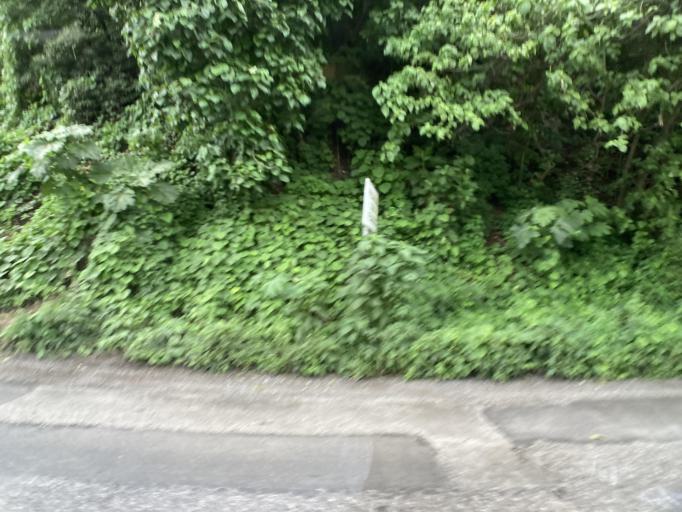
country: GT
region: Guatemala
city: Villa Canales
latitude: 14.4351
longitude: -90.5355
